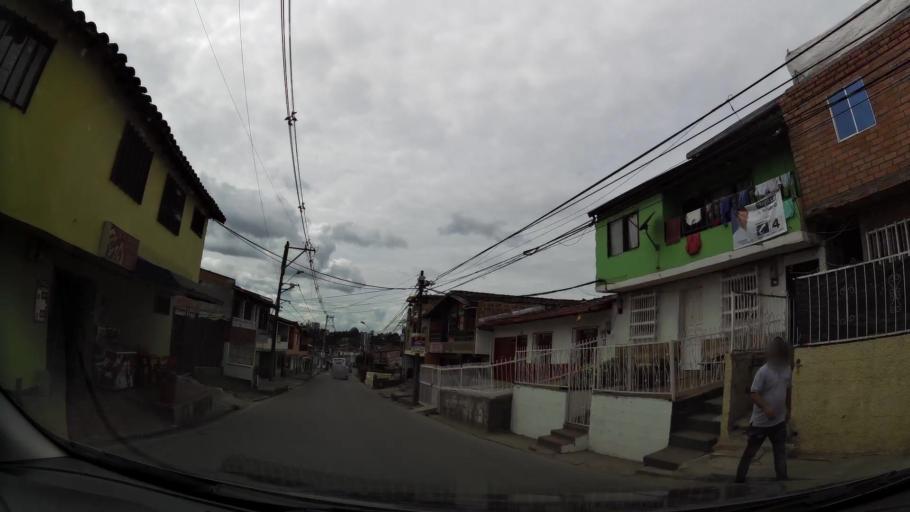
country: CO
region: Antioquia
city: Rionegro
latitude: 6.1537
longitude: -75.3646
